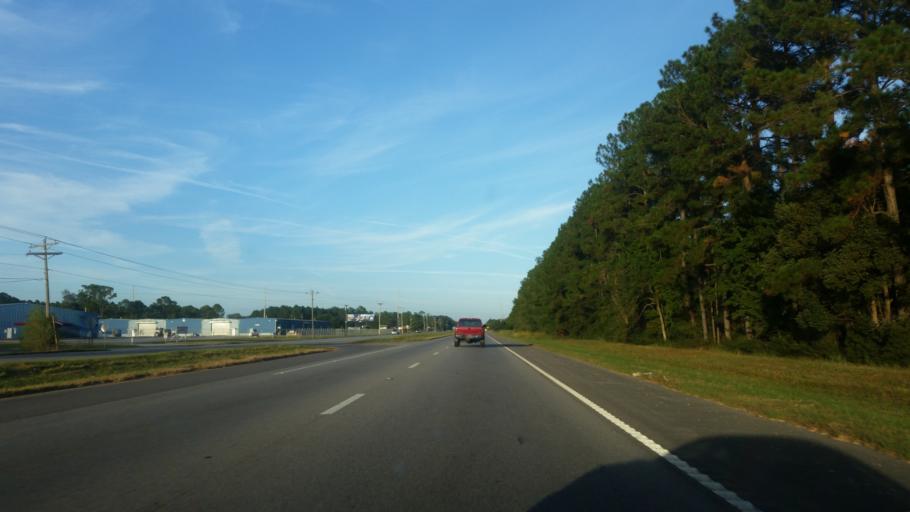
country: US
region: Mississippi
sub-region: Jackson County
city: Moss Point
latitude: 30.3948
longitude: -88.5003
